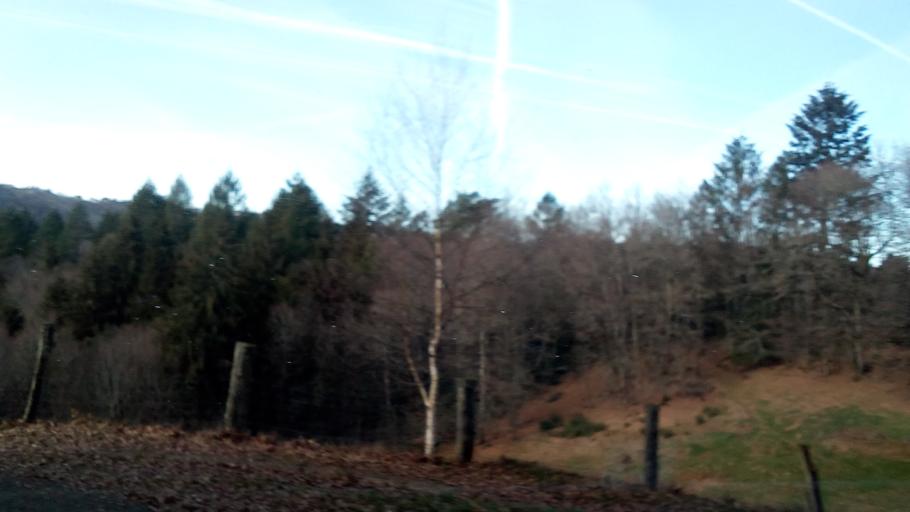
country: FR
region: Limousin
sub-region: Departement de la Correze
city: Naves
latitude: 45.3104
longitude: 1.7915
